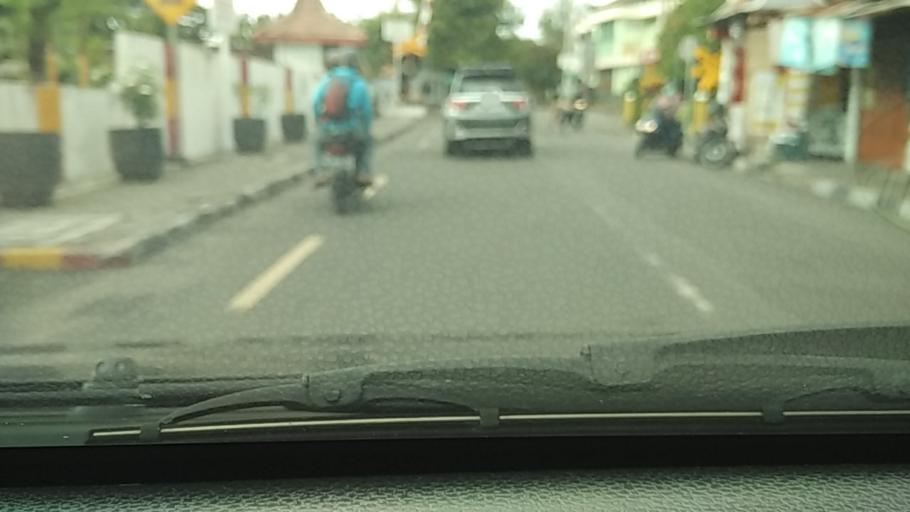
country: ID
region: Daerah Istimewa Yogyakarta
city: Yogyakarta
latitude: -7.7896
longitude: 110.3865
